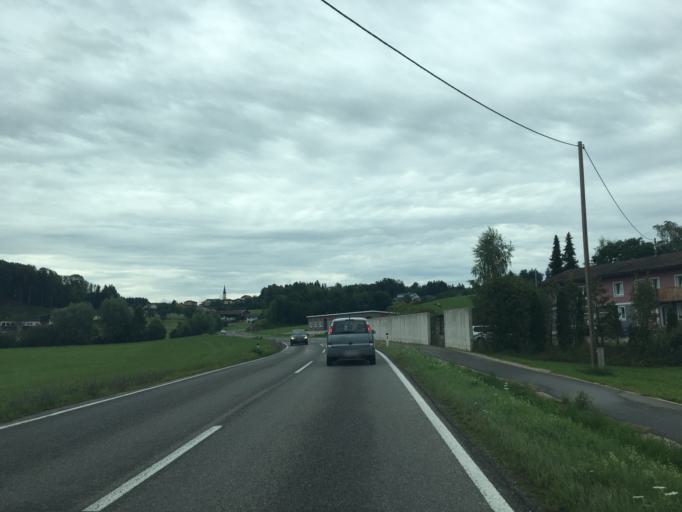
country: AT
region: Salzburg
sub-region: Politischer Bezirk Salzburg-Umgebung
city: Dorfbeuern
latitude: 48.0635
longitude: 12.9880
